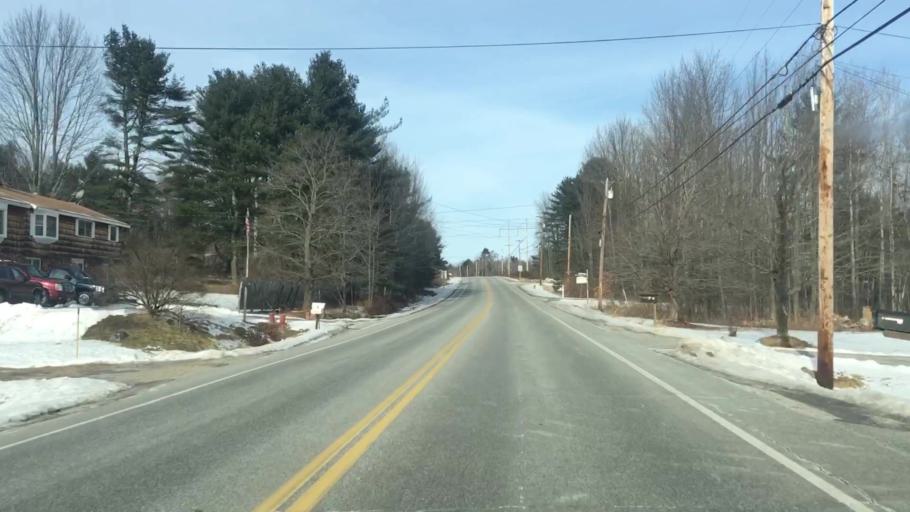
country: US
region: Maine
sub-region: Cumberland County
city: South Windham
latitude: 43.7495
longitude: -70.4248
